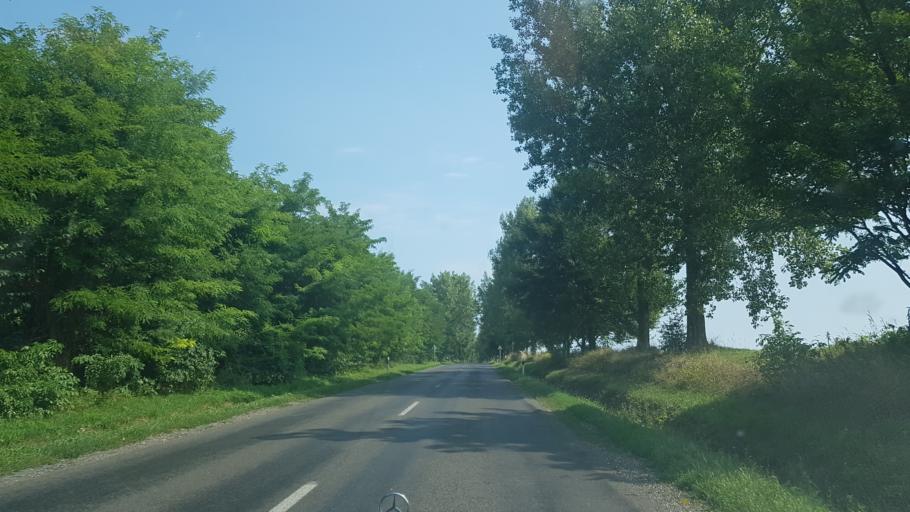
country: HU
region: Somogy
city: Bohonye
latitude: 46.3891
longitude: 17.3753
